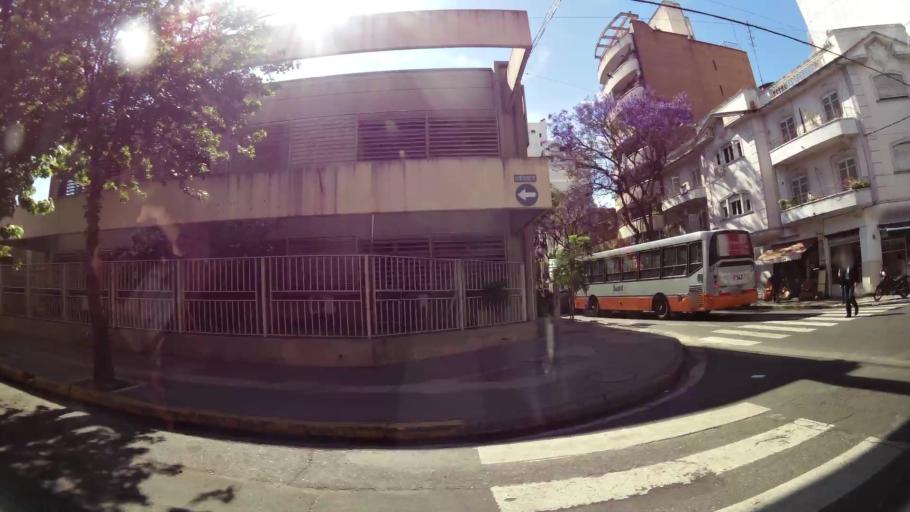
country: AR
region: Santa Fe
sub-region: Departamento de Rosario
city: Rosario
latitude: -32.9563
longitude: -60.6392
